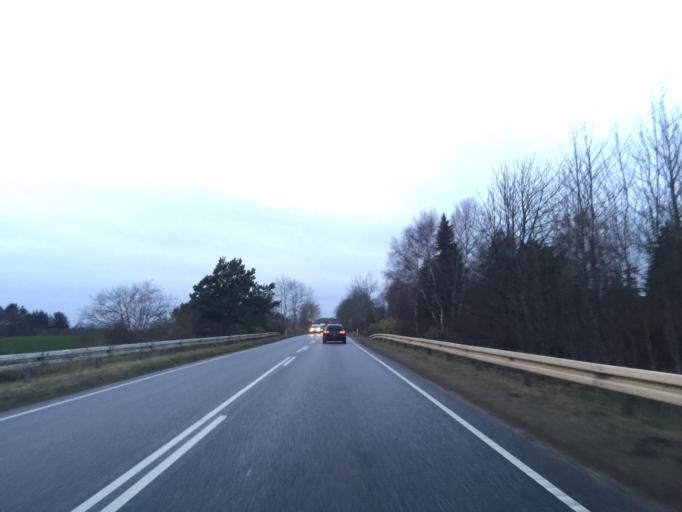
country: DK
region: Central Jutland
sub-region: Viborg Kommune
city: Bjerringbro
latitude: 56.3103
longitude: 9.5609
